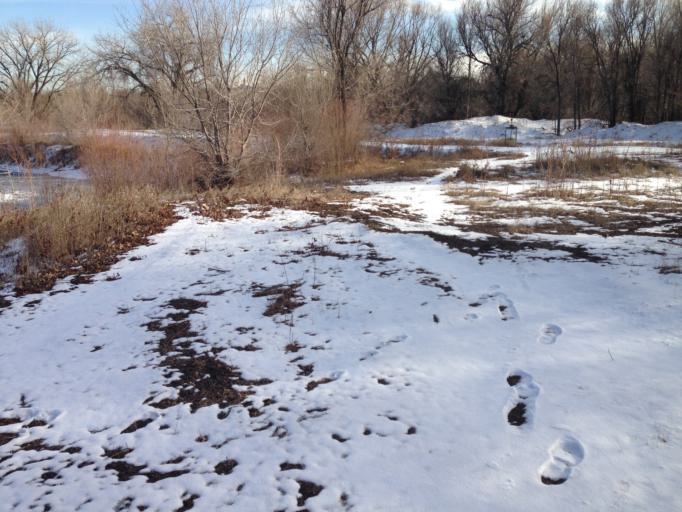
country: US
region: Colorado
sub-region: Adams County
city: Berkley
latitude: 39.7974
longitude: -105.0433
